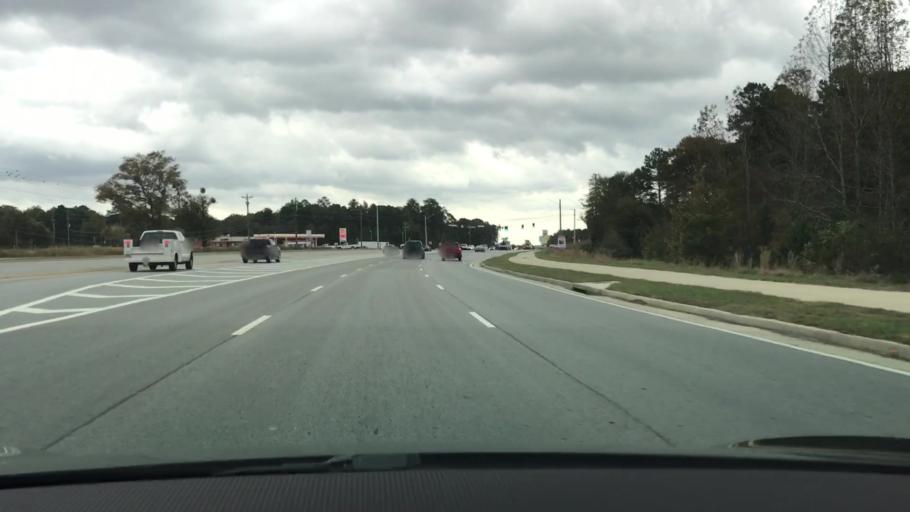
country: US
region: Georgia
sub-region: Hall County
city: Flowery Branch
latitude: 34.1346
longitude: -83.9377
